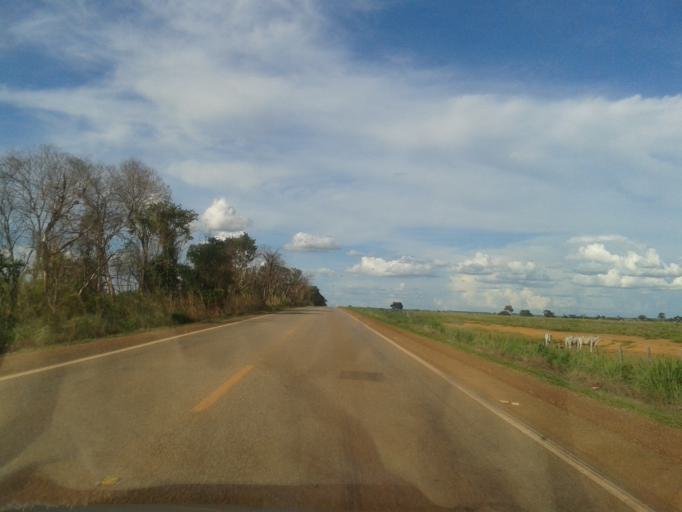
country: BR
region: Goias
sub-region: Mozarlandia
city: Mozarlandia
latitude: -14.3927
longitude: -50.4395
